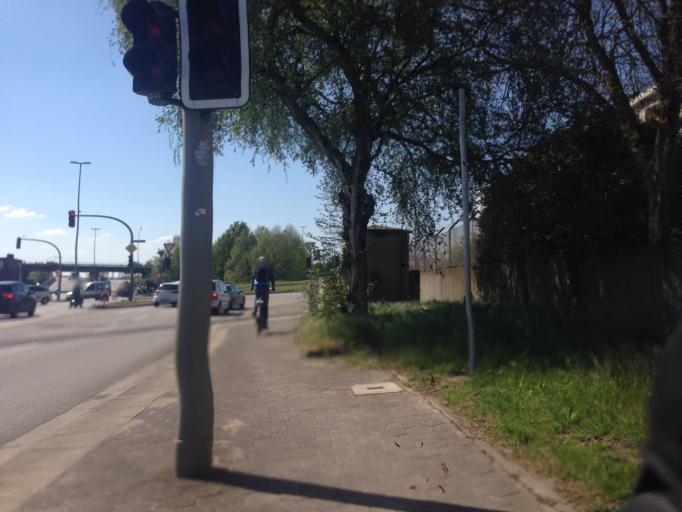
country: DE
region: Hamburg
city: Kleiner Grasbrook
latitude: 53.5278
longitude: 9.9806
